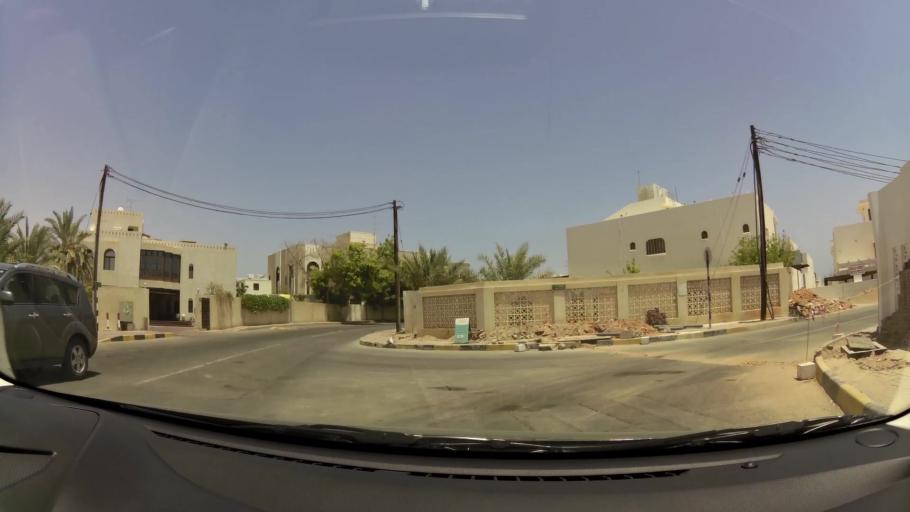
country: OM
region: Muhafazat Masqat
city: Bawshar
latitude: 23.6088
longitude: 58.4714
